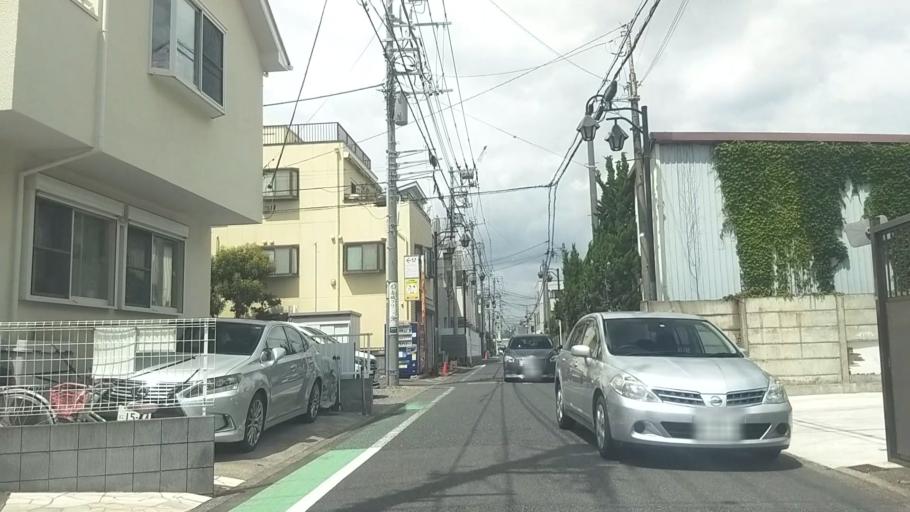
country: JP
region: Kanagawa
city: Fujisawa
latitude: 35.3397
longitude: 139.4515
